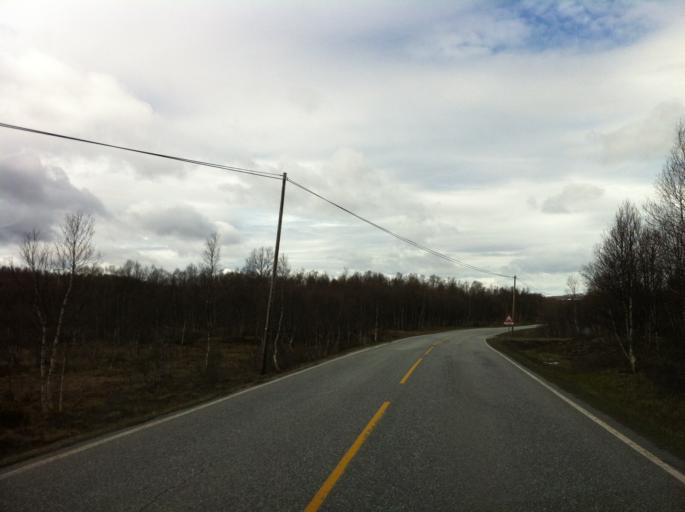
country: NO
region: Sor-Trondelag
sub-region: Roros
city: Roros
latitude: 62.5990
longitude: 11.6855
